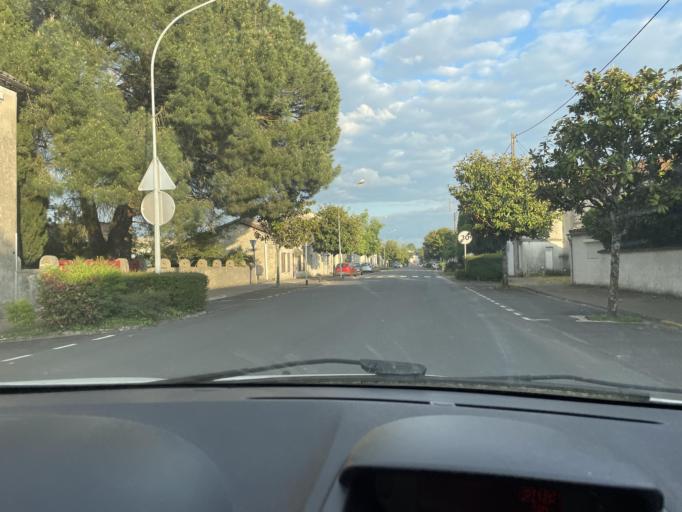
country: FR
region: Aquitaine
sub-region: Departement du Lot-et-Garonne
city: Casteljaloux
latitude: 44.3165
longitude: 0.0822
